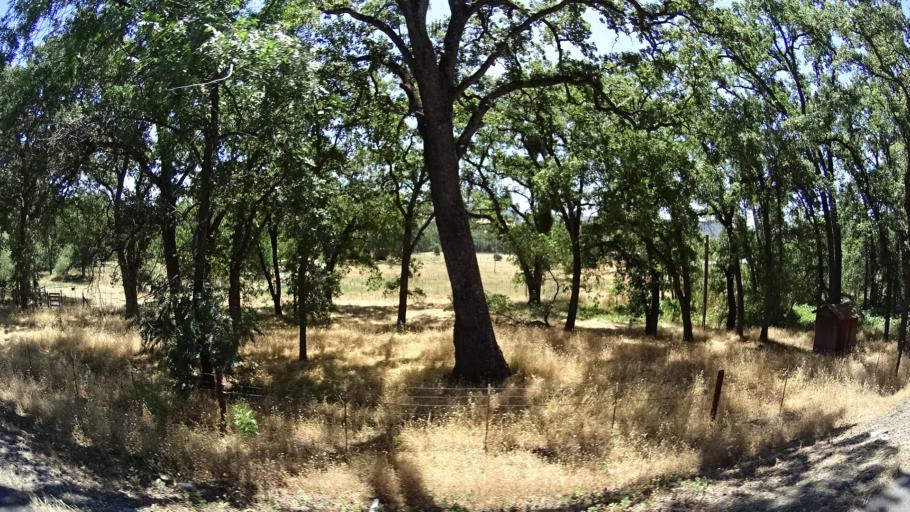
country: US
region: California
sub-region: Calaveras County
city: Angels Camp
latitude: 38.0977
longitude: -120.5297
